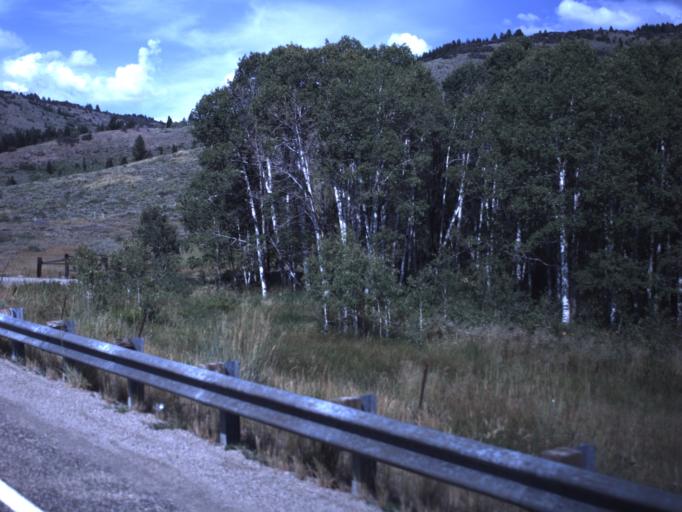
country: US
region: Utah
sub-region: Cache County
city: Richmond
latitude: 41.9190
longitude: -111.5614
